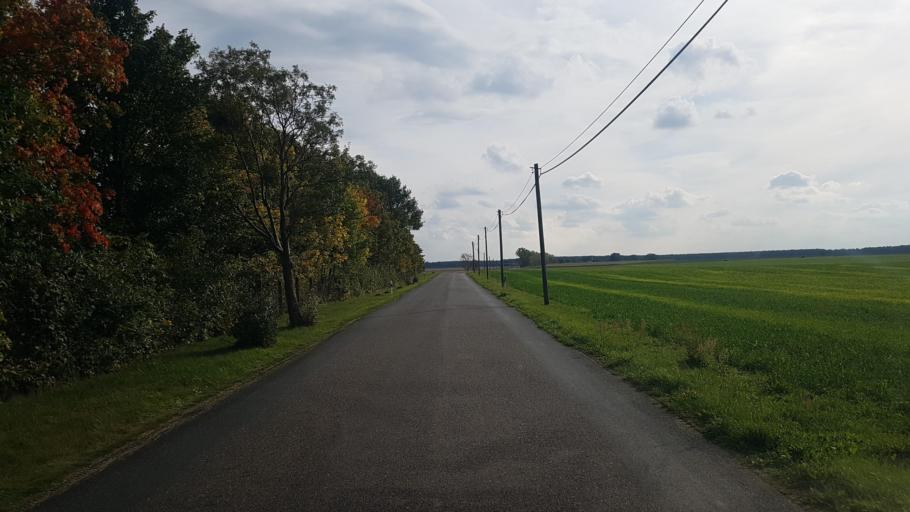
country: DE
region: Brandenburg
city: Dahme
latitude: 51.8768
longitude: 13.3829
